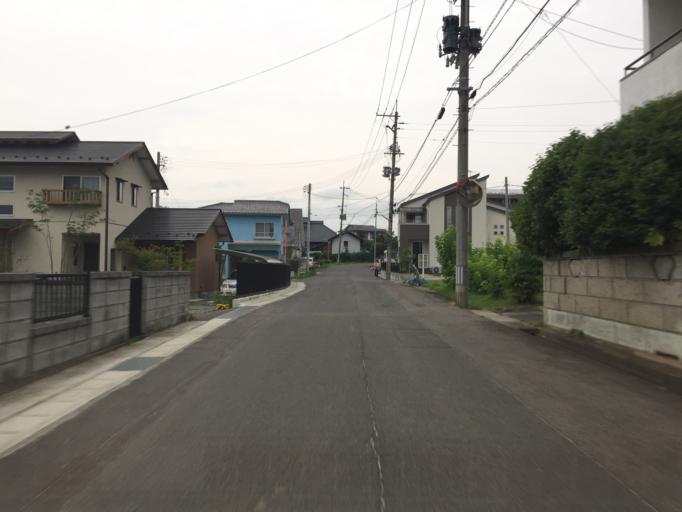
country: JP
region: Fukushima
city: Fukushima-shi
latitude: 37.7159
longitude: 140.4563
